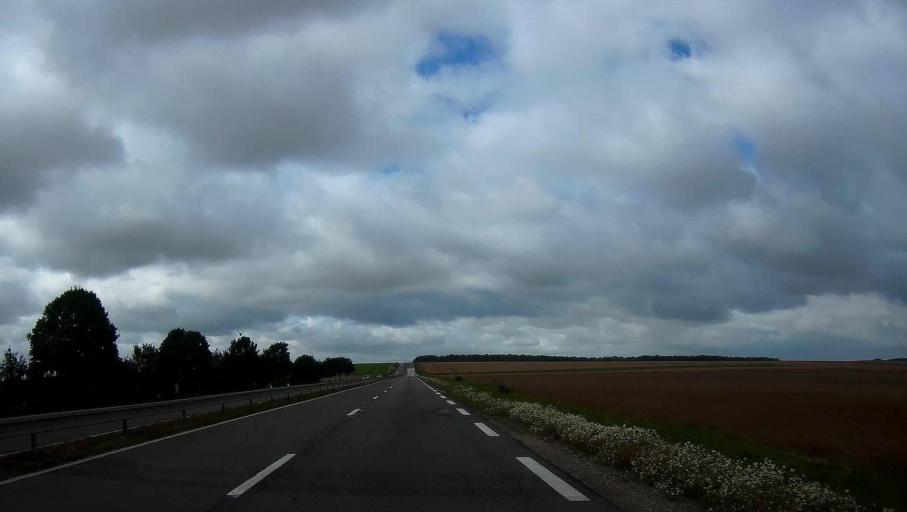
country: FR
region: Champagne-Ardenne
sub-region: Departement de la Marne
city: Warmeriville
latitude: 49.4036
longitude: 4.2484
